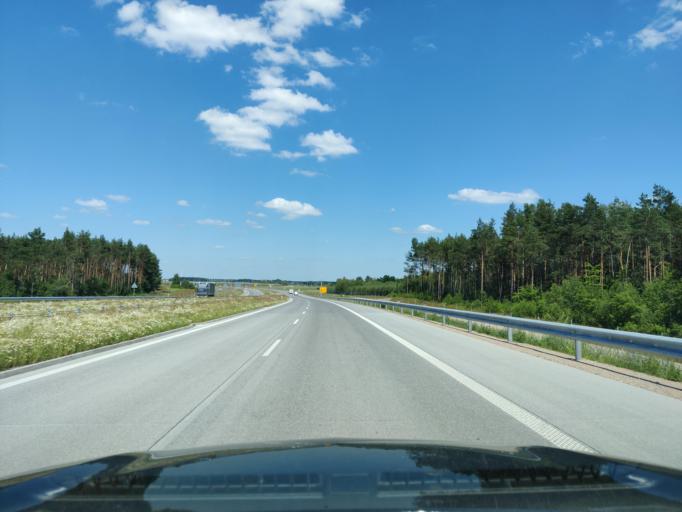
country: PL
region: Masovian Voivodeship
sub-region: Powiat mlawski
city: Wisniewo
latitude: 52.9813
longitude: 20.3391
